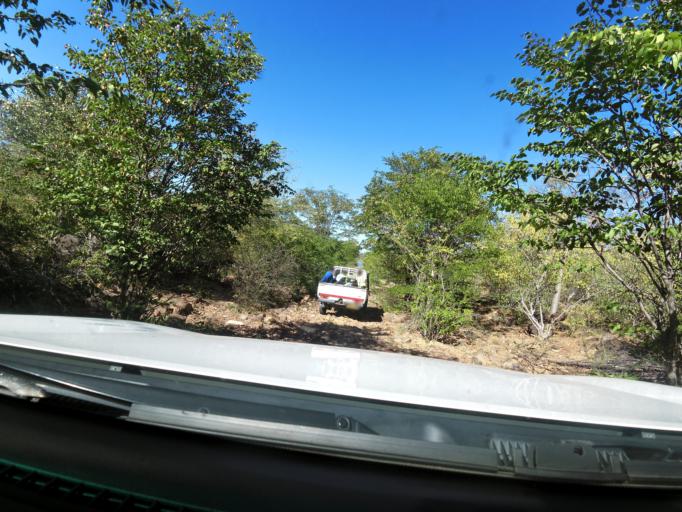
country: ZW
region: Matabeleland North
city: Kamativi Mine
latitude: -17.9427
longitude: 27.0770
